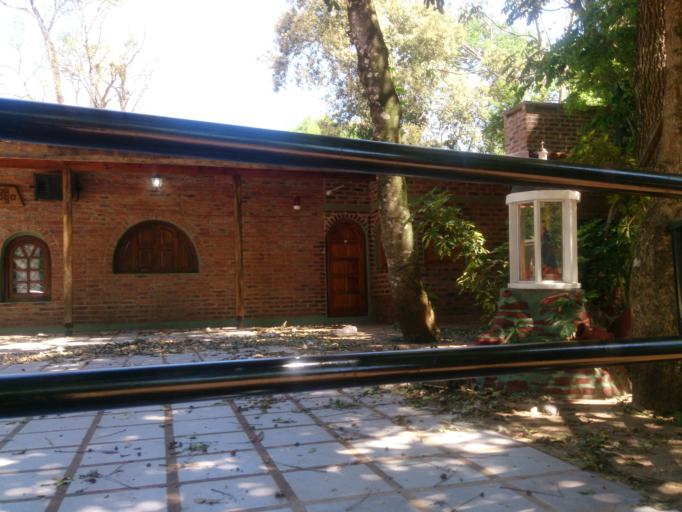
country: AR
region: Misiones
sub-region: Departamento de Obera
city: Obera
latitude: -27.5004
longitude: -55.1132
